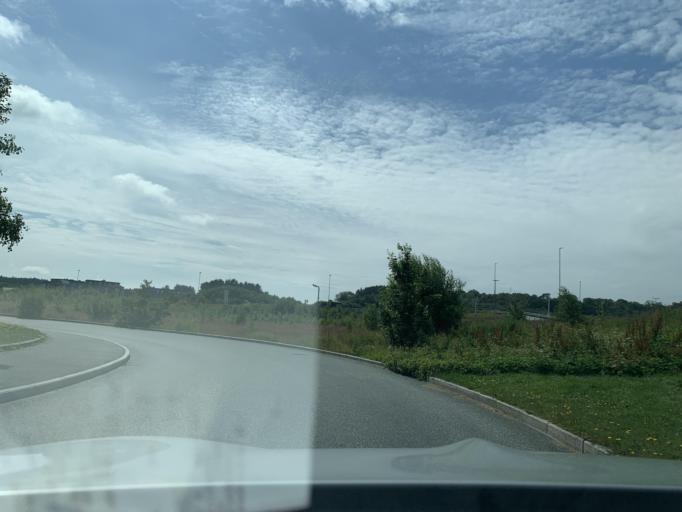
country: NO
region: Rogaland
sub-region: Sola
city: Sola
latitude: 58.8969
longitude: 5.6794
